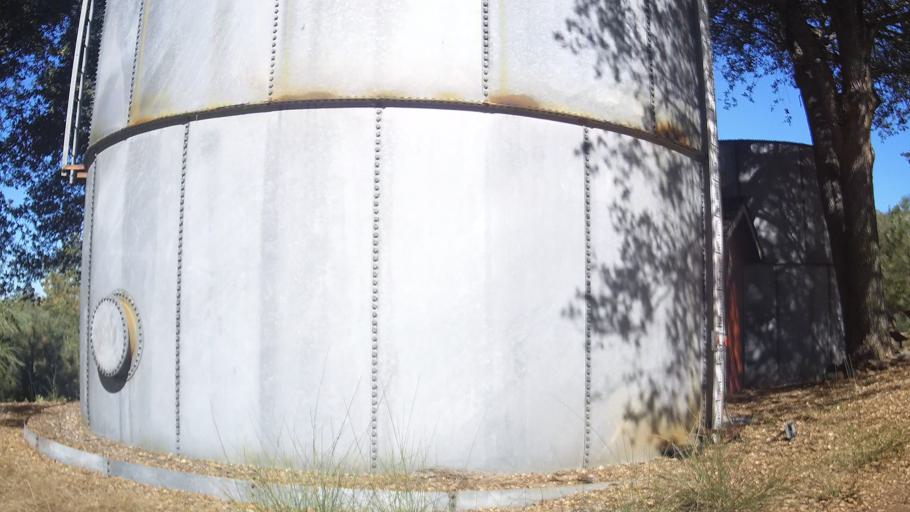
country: US
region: California
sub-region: San Diego County
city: Julian
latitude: 33.0373
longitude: -116.6268
